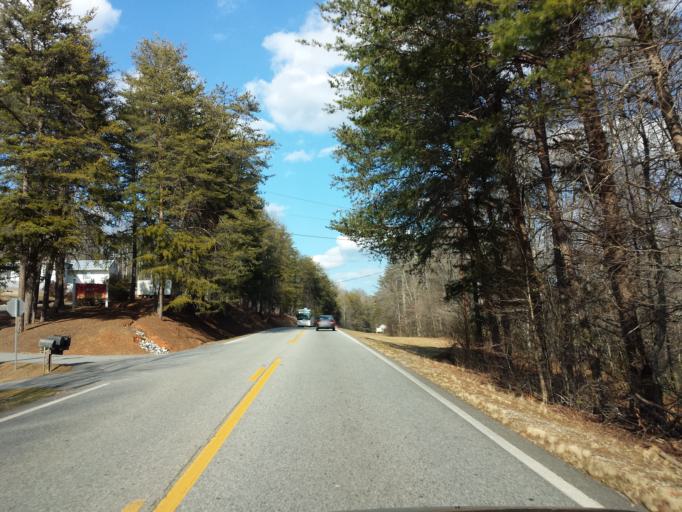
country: US
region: Georgia
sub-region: Lumpkin County
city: Dahlonega
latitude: 34.4992
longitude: -83.9387
